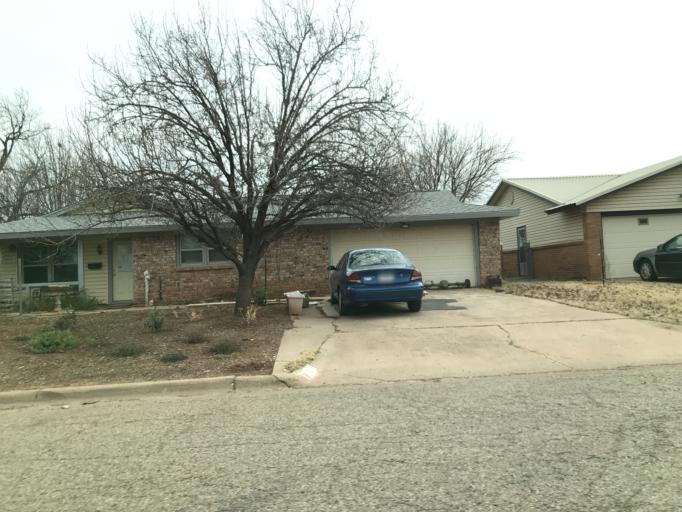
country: US
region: Texas
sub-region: Taylor County
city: Abilene
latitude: 32.4726
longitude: -99.7621
